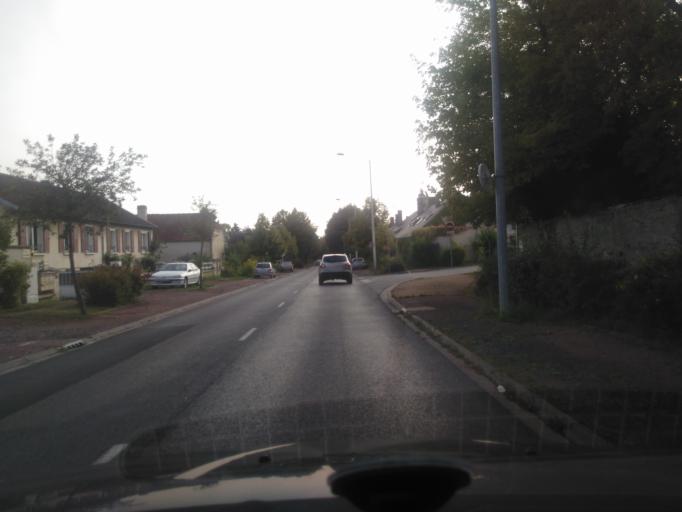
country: FR
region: Picardie
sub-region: Departement de l'Aisne
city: Laon
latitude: 49.5523
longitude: 3.6054
